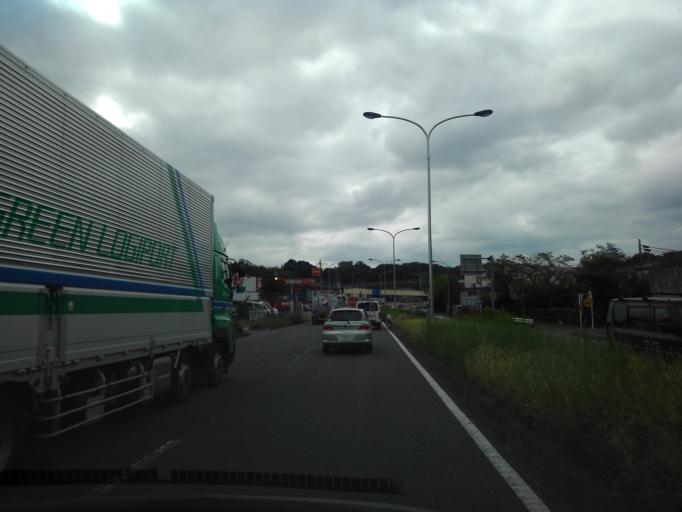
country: JP
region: Tokyo
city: Hachioji
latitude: 35.6822
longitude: 139.3443
